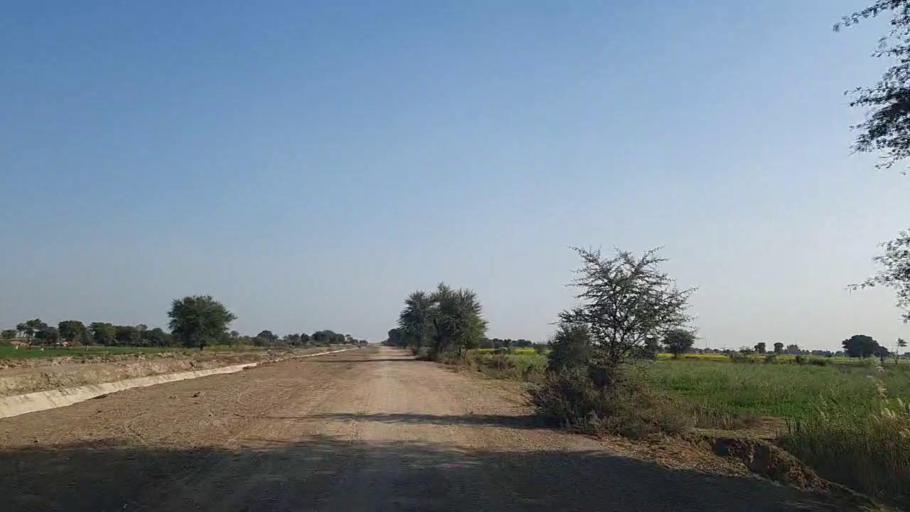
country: PK
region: Sindh
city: Shahpur Chakar
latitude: 26.2006
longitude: 68.6490
